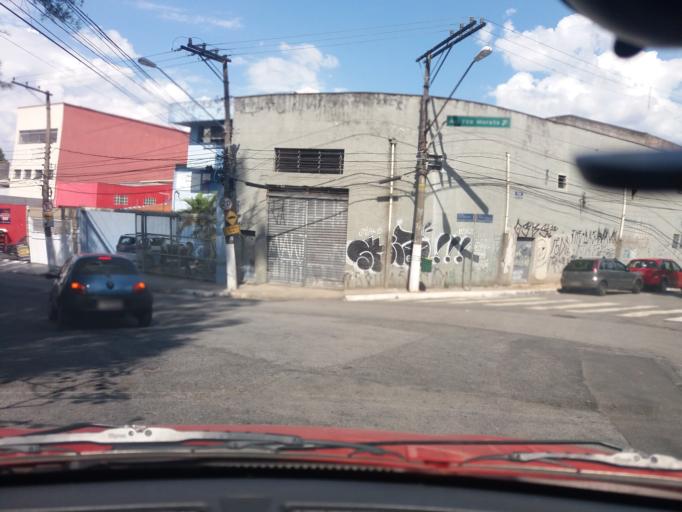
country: BR
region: Sao Paulo
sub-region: Taboao Da Serra
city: Taboao da Serra
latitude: -23.5892
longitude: -46.7380
